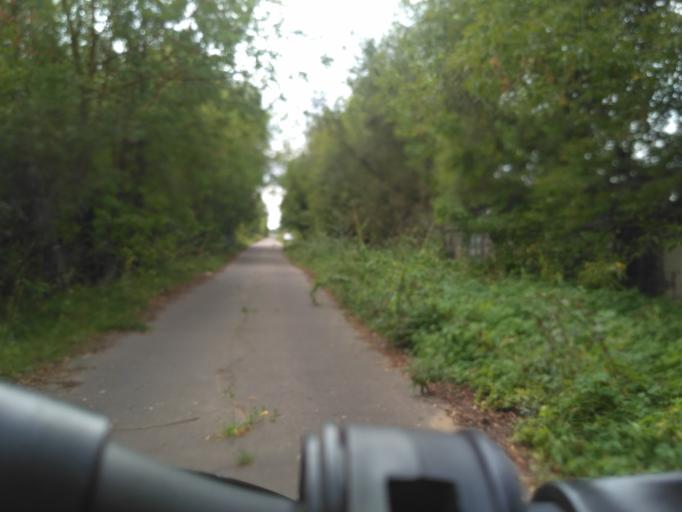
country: RU
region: Moskovskaya
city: Dubna
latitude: 56.7362
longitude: 37.1475
